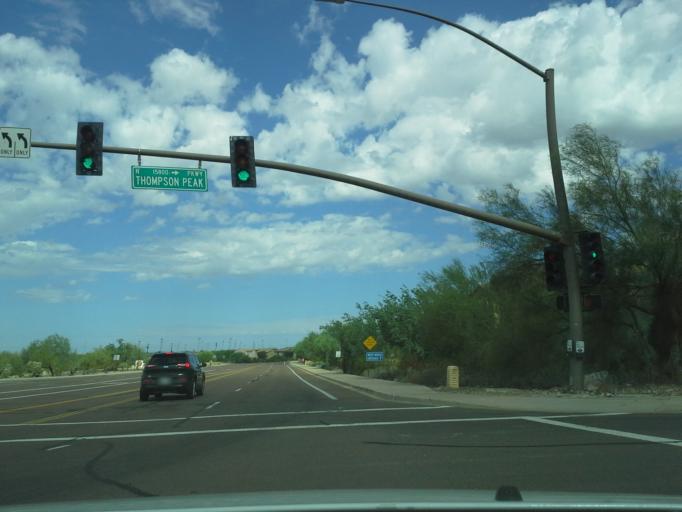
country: US
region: Arizona
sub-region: Maricopa County
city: Scottsdale
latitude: 33.6293
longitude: -111.8633
